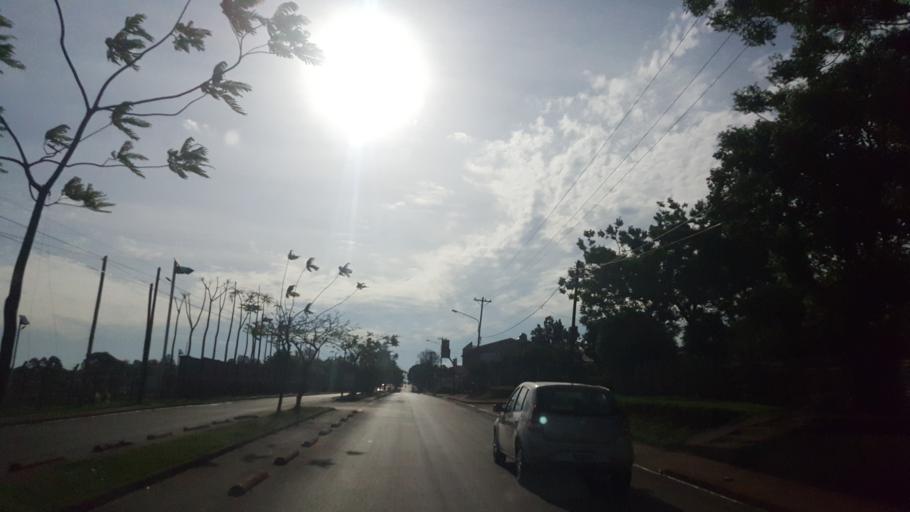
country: AR
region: Misiones
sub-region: Departamento de Capital
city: Posadas
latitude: -27.4275
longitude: -55.9156
